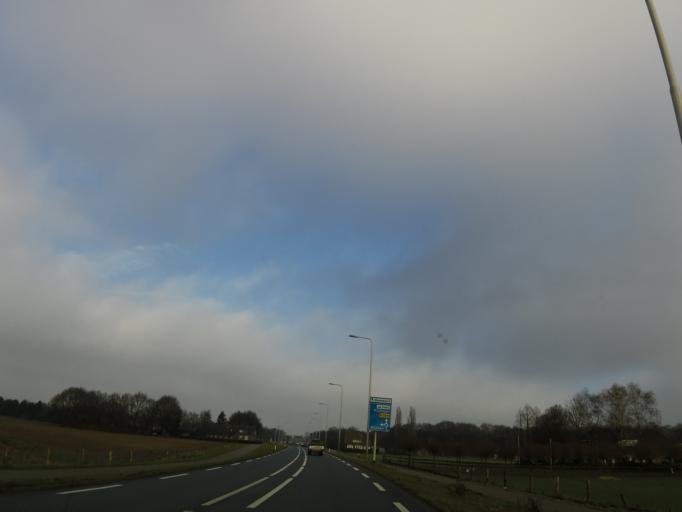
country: NL
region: Gelderland
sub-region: Gemeente Wijchen
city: Wijchen
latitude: 51.7941
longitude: 5.7521
